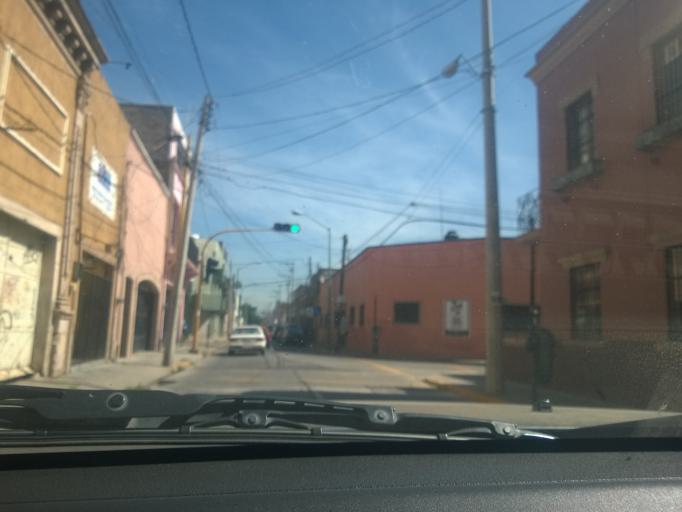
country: MX
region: Guanajuato
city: Leon
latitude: 21.1283
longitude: -101.6828
